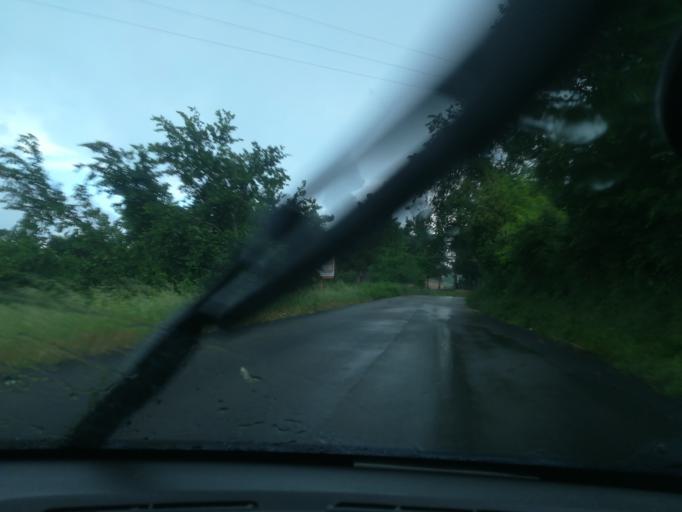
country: IT
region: The Marches
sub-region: Provincia di Macerata
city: Casette Verdini
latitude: 43.2873
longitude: 13.3905
